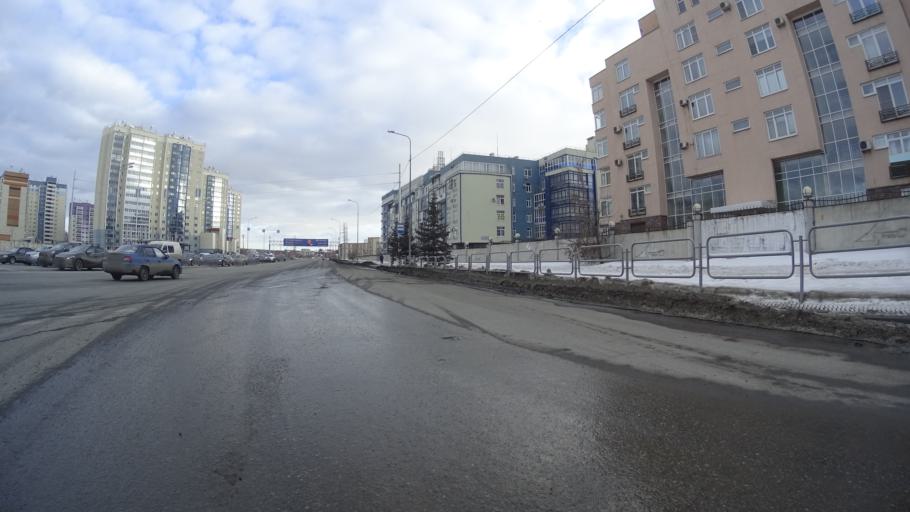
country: RU
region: Chelyabinsk
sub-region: Gorod Chelyabinsk
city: Chelyabinsk
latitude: 55.1601
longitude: 61.3022
